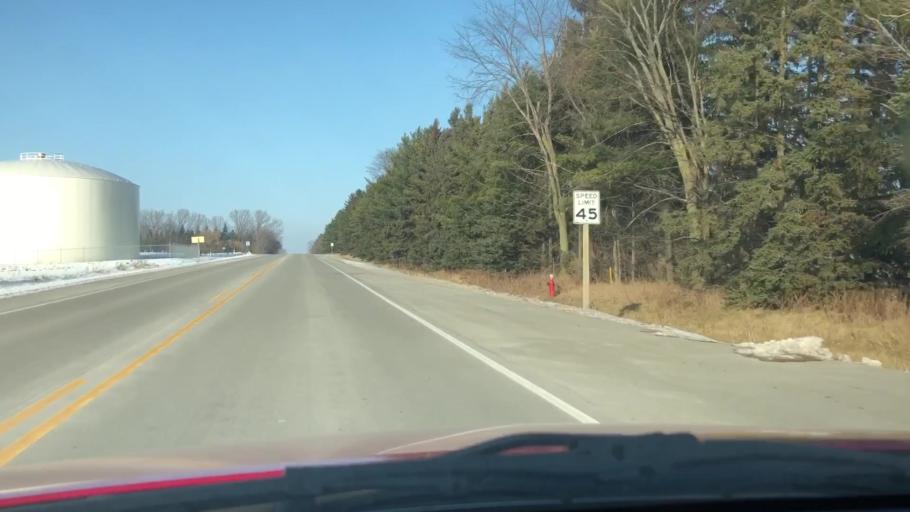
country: US
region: Wisconsin
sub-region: Outagamie County
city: Kimberly
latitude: 44.3344
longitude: -88.3748
